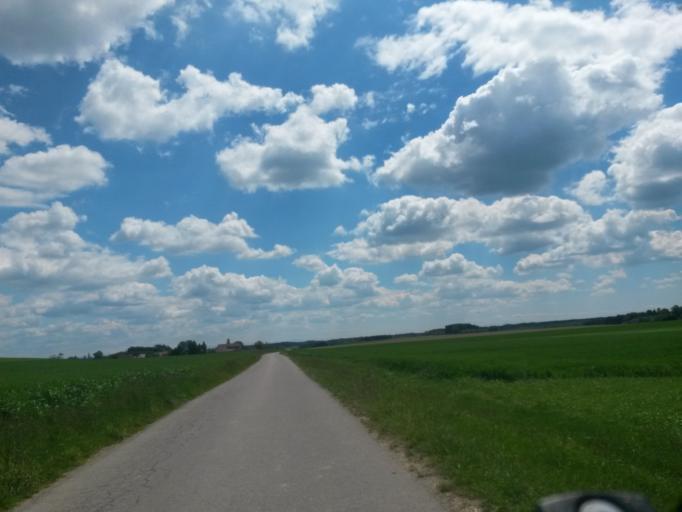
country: DE
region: Baden-Wuerttemberg
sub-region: Tuebingen Region
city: Ingoldingen
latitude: 47.9922
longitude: 9.7111
